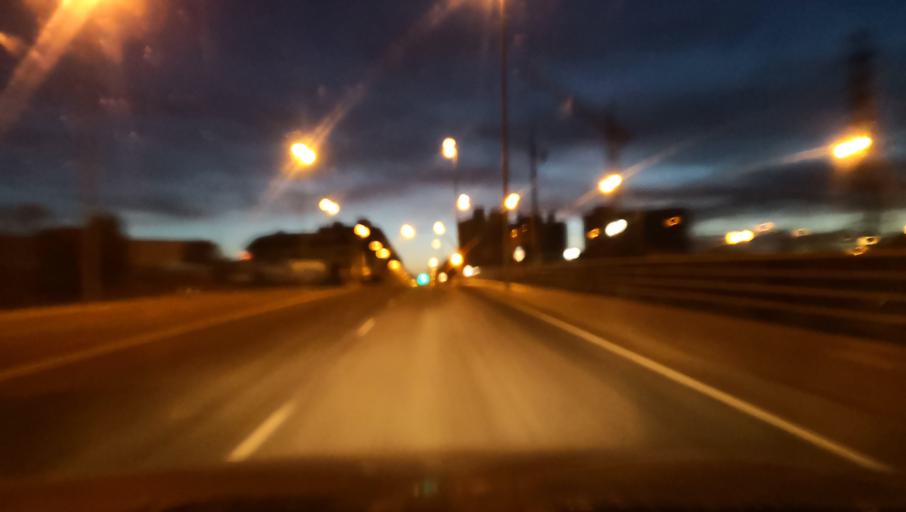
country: ES
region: Castille and Leon
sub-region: Provincia de Zamora
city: Zamora
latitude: 41.5173
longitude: -5.7263
